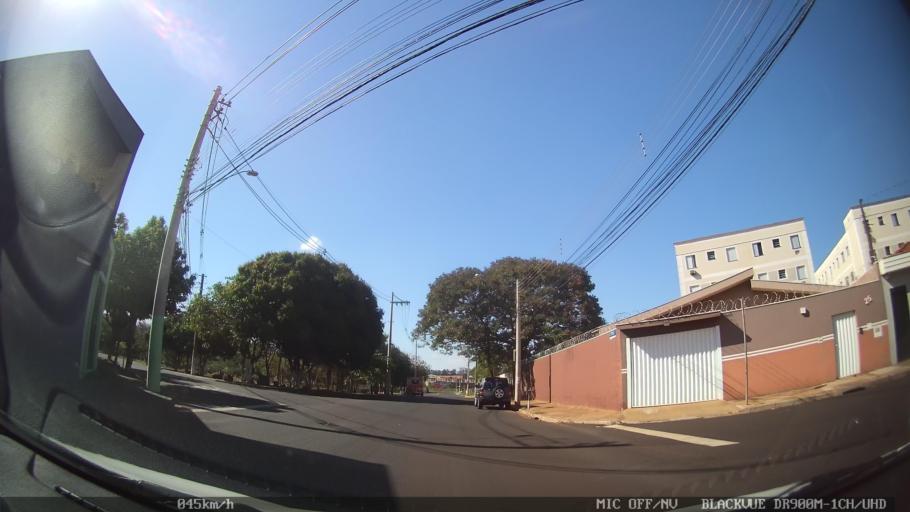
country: BR
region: Sao Paulo
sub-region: Ribeirao Preto
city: Ribeirao Preto
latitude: -21.2174
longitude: -47.7634
